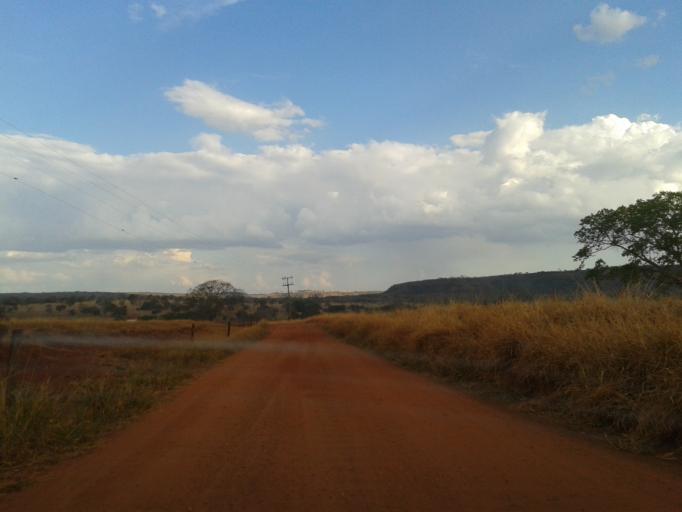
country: BR
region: Minas Gerais
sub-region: Ituiutaba
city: Ituiutaba
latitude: -19.1938
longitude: -49.8444
